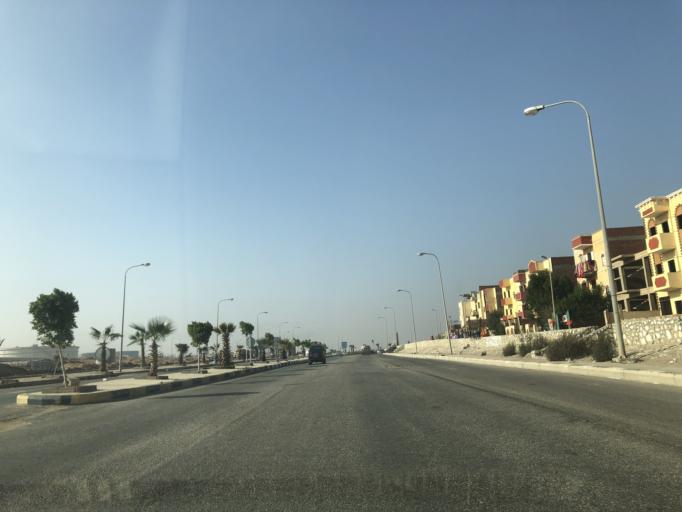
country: EG
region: Al Jizah
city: Madinat Sittah Uktubar
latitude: 29.9314
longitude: 31.0460
